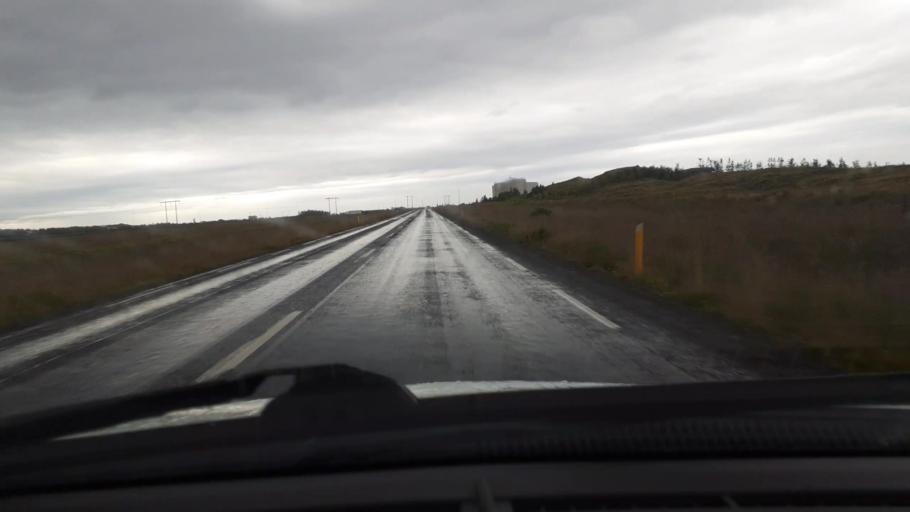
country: IS
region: West
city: Akranes
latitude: 64.3352
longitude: -22.0297
